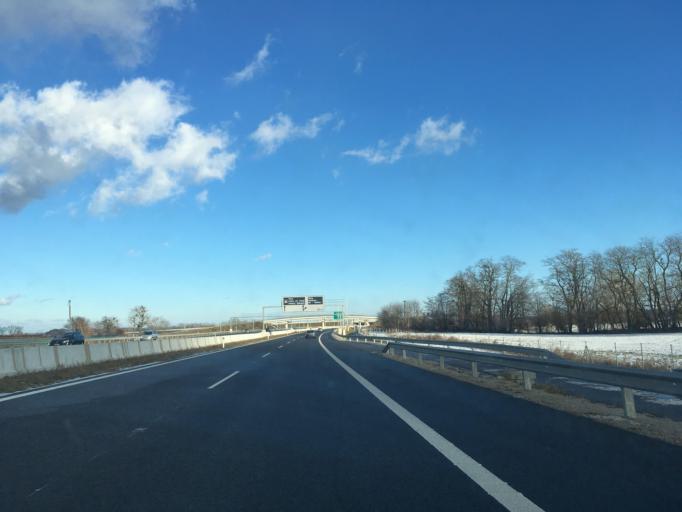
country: SK
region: Bratislavsky
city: Dunajska Luzna
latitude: 48.0890
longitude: 17.1740
